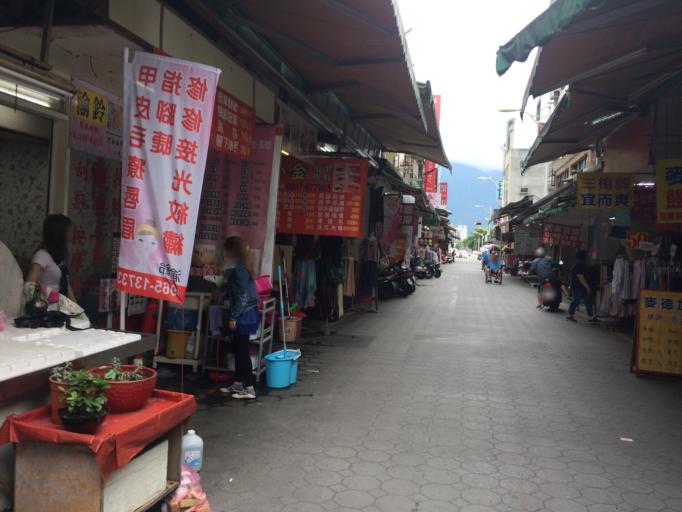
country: TW
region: Taiwan
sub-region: Hualien
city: Hualian
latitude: 23.9778
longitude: 121.6099
